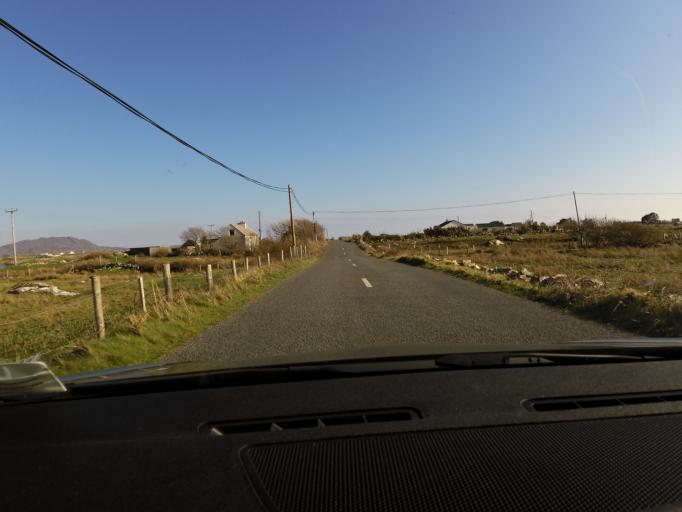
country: IE
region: Connaught
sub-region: County Galway
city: Clifden
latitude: 53.4204
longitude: -10.0625
